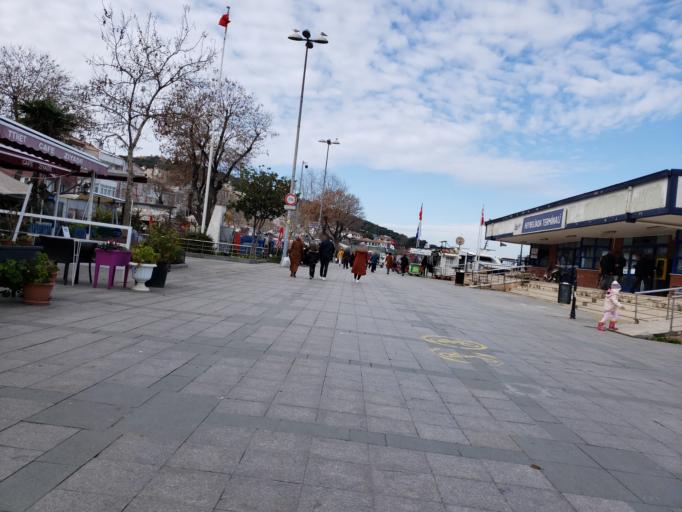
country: TR
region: Istanbul
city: Adalan
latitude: 40.8775
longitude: 29.1008
